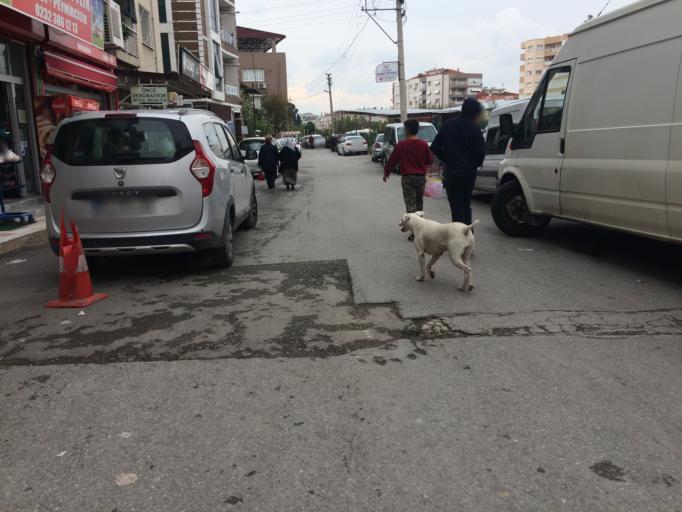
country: TR
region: Izmir
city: Karsiyaka
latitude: 38.4929
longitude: 27.0601
